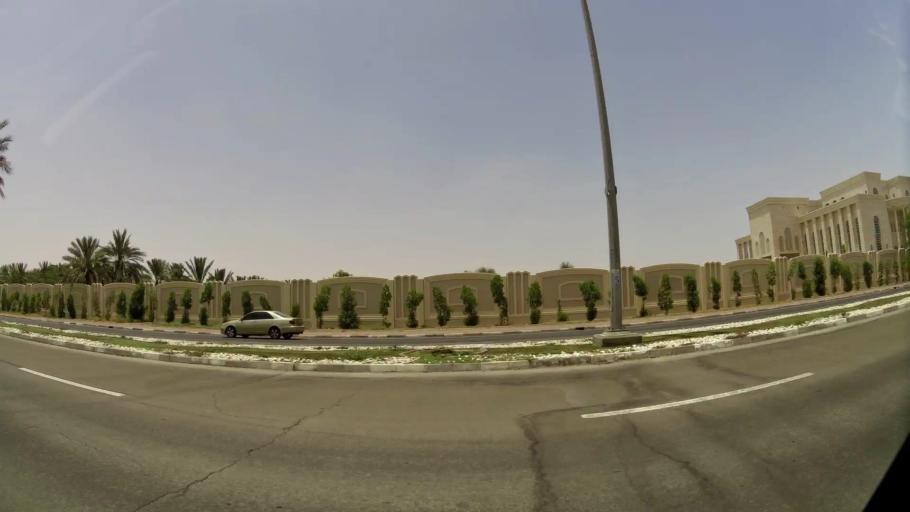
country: AE
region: Abu Dhabi
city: Al Ain
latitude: 24.2119
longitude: 55.7279
